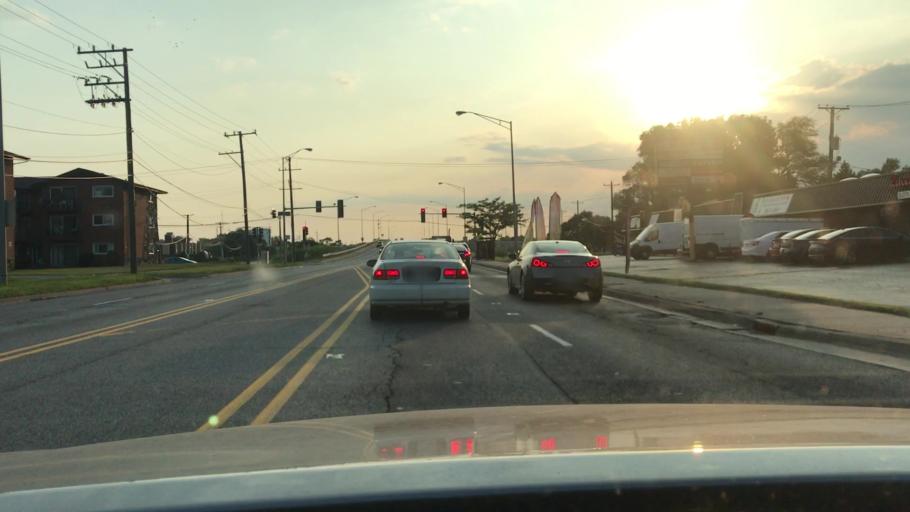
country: US
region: Illinois
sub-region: Cook County
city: Bridgeview
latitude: 41.7481
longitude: -87.8033
